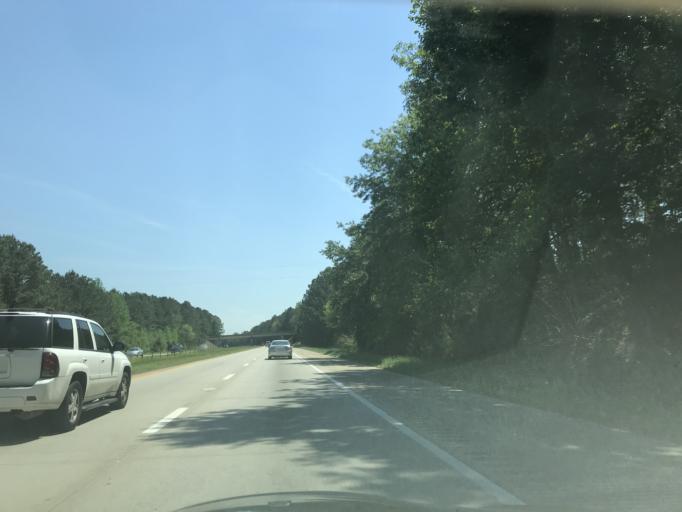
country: US
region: North Carolina
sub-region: Johnston County
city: Benson
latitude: 35.4753
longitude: -78.5500
